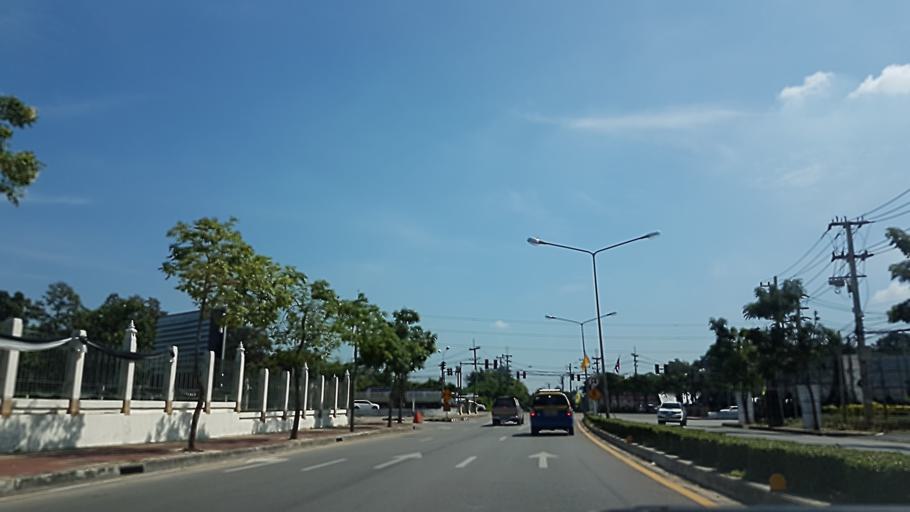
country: TH
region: Chiang Mai
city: Chiang Mai
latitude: 18.8234
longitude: 98.9644
